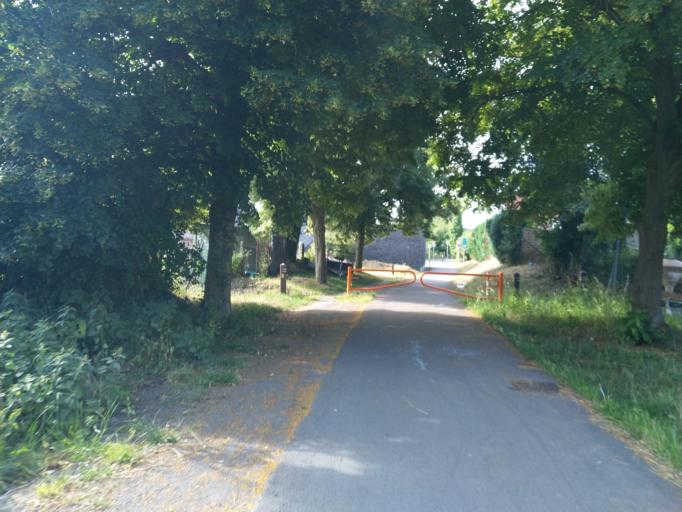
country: BE
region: Wallonia
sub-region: Province du Hainaut
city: Erquelinnes
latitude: 50.3114
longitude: 4.1199
